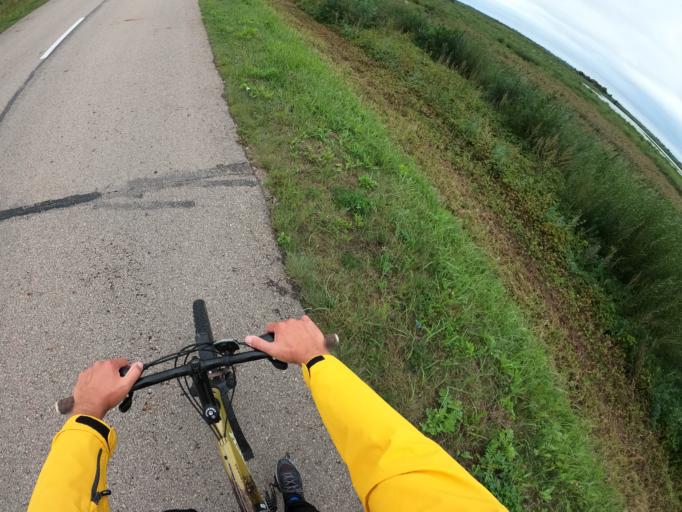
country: LT
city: Rusne
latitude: 55.3429
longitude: 21.3462
